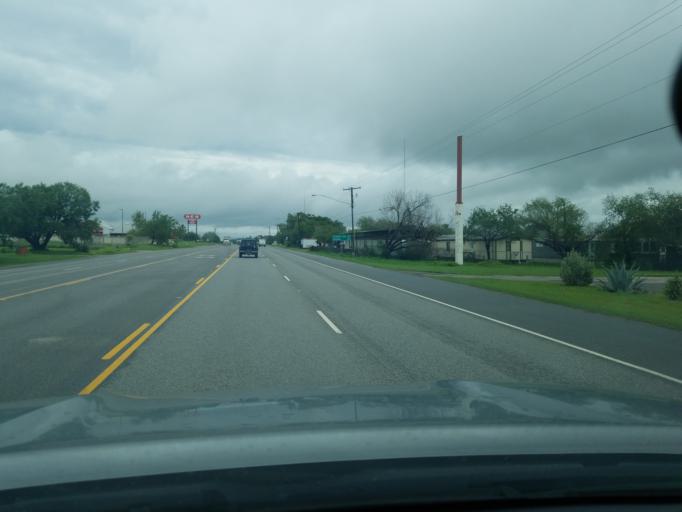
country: US
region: Texas
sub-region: Dimmit County
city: Carrizo Springs
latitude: 28.5339
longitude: -99.8518
